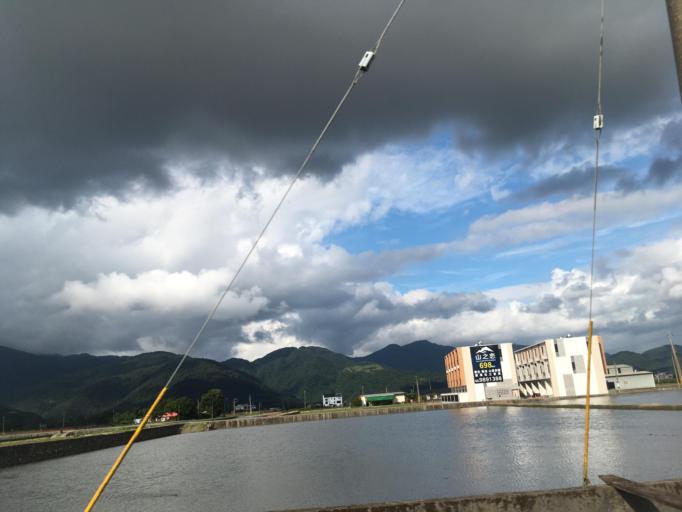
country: TW
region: Taiwan
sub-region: Yilan
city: Yilan
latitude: 24.6675
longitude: 121.6330
